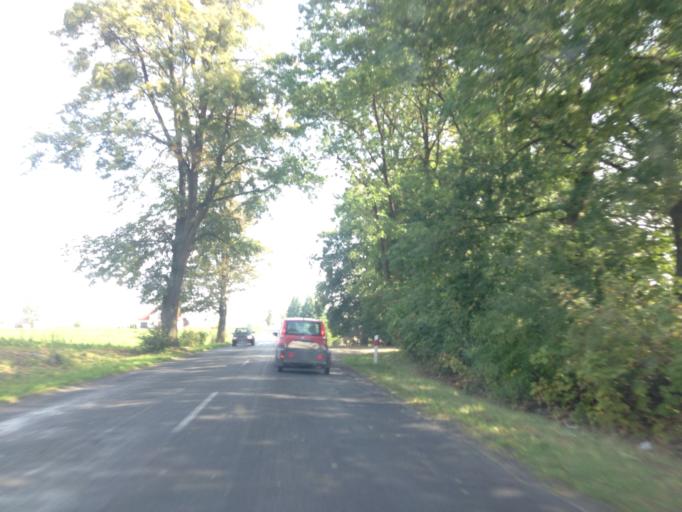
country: PL
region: Kujawsko-Pomorskie
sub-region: Powiat brodnicki
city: Brodnica
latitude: 53.2425
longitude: 19.4783
